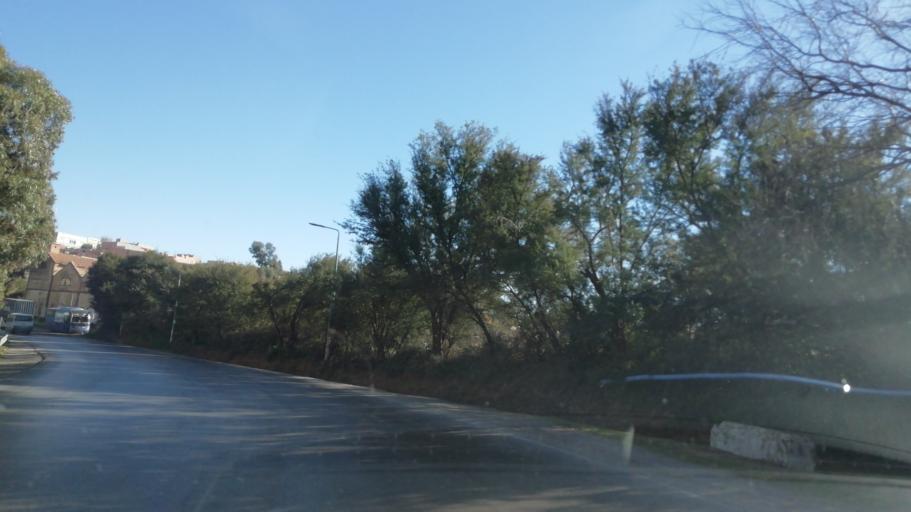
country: DZ
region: Relizane
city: Smala
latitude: 35.6562
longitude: 0.8185
